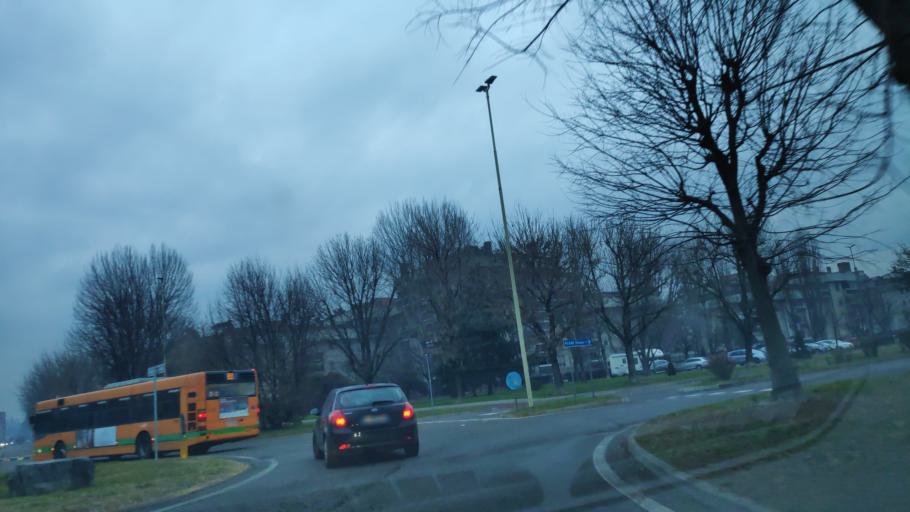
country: IT
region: Lombardy
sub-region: Citta metropolitana di Milano
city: Romano Banco
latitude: 45.4295
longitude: 9.1222
